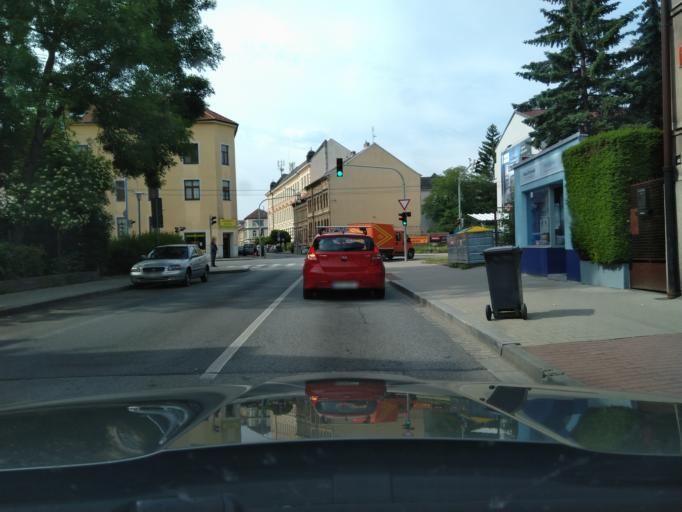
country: CZ
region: Jihocesky
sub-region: Okres Ceske Budejovice
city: Ceske Budejovice
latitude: 48.9835
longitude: 14.4777
